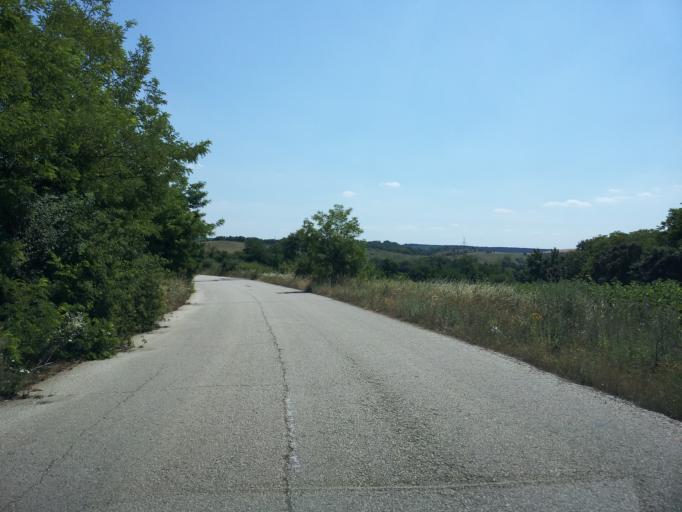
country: HU
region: Fejer
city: Szarliget
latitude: 47.5258
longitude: 18.5691
